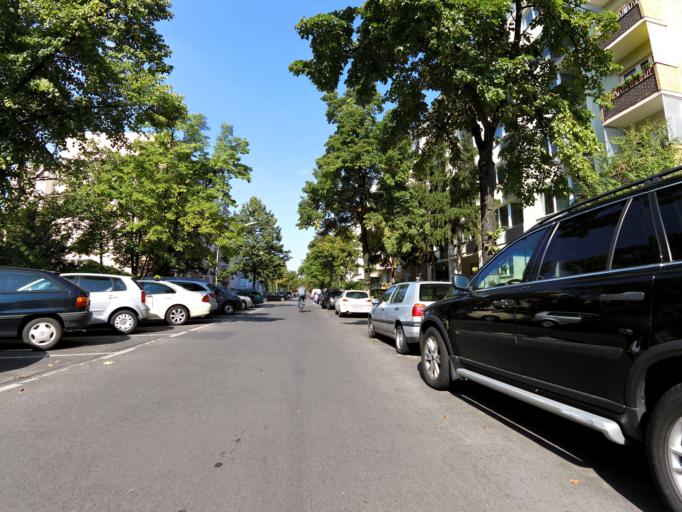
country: DE
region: Berlin
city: Berlin Schoeneberg
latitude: 52.4881
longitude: 13.3331
